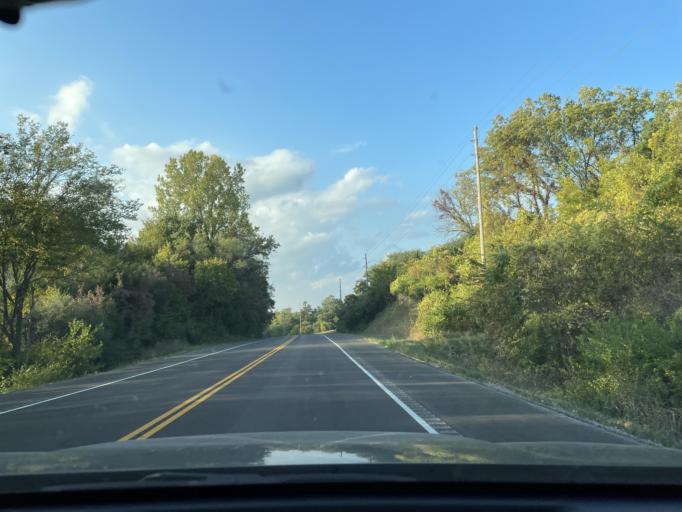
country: US
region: Missouri
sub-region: Andrew County
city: Country Club Village
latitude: 39.8504
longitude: -94.8699
